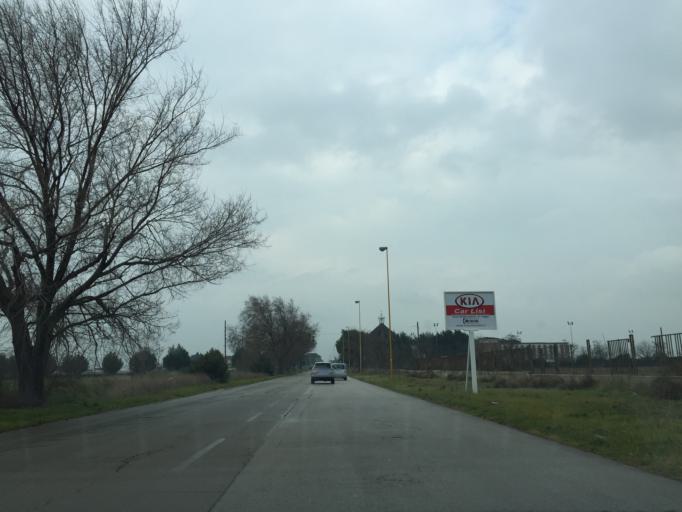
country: IT
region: Apulia
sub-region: Provincia di Foggia
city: Foggia
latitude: 41.4503
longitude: 15.5156
